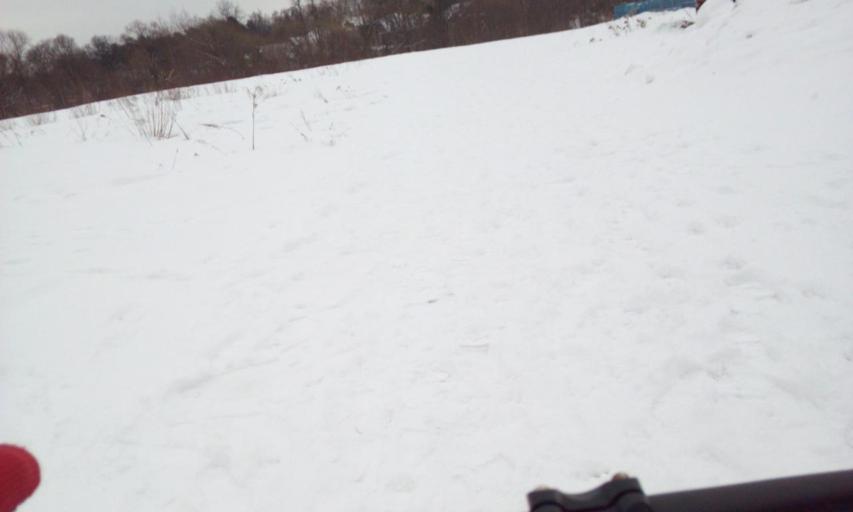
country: RU
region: Moskovskaya
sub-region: Leninskiy Rayon
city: Vnukovo
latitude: 55.6139
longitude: 37.3109
